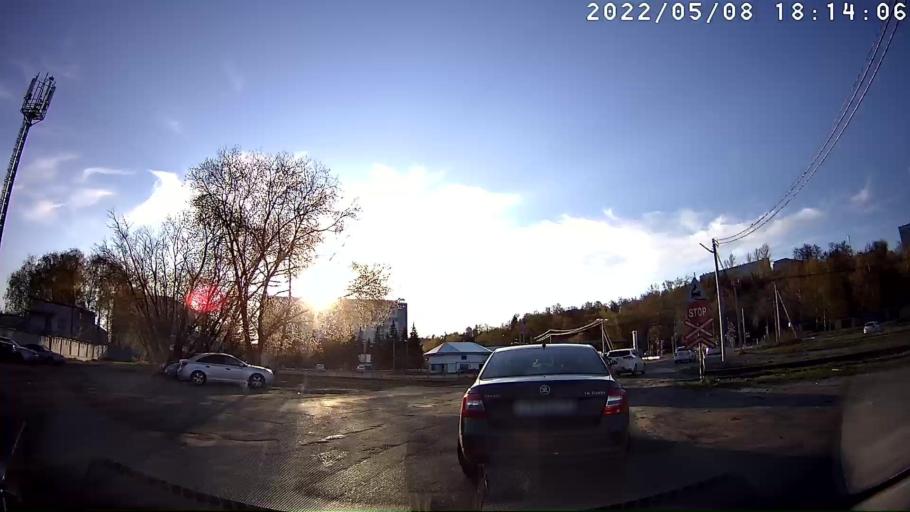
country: RU
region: Tatarstan
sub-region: Zelenodol'skiy Rayon
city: Zelenodolsk
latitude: 55.8415
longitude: 48.4928
